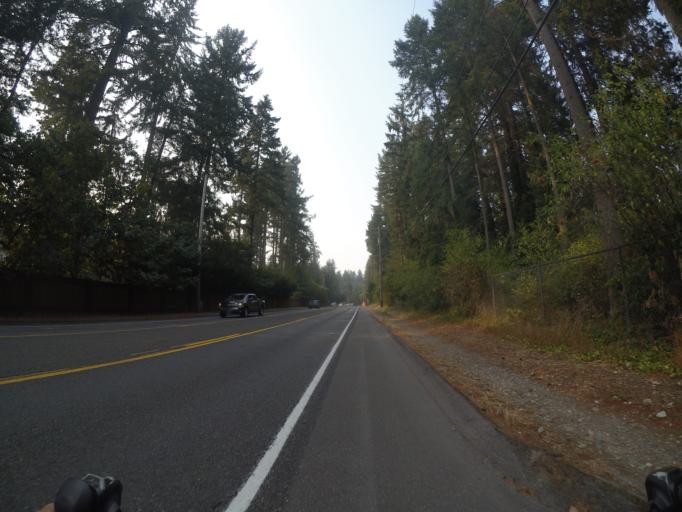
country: US
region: Washington
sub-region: Pierce County
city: Lakewood
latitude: 47.1532
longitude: -122.5234
